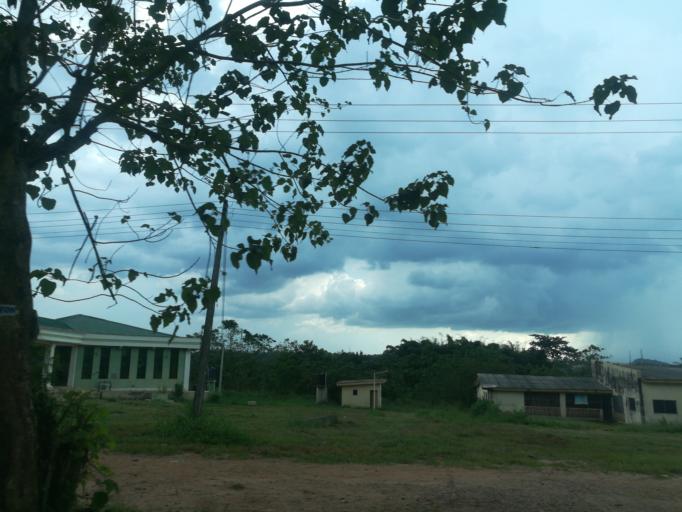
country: NG
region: Oyo
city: Ibadan
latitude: 7.4367
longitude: 3.8852
